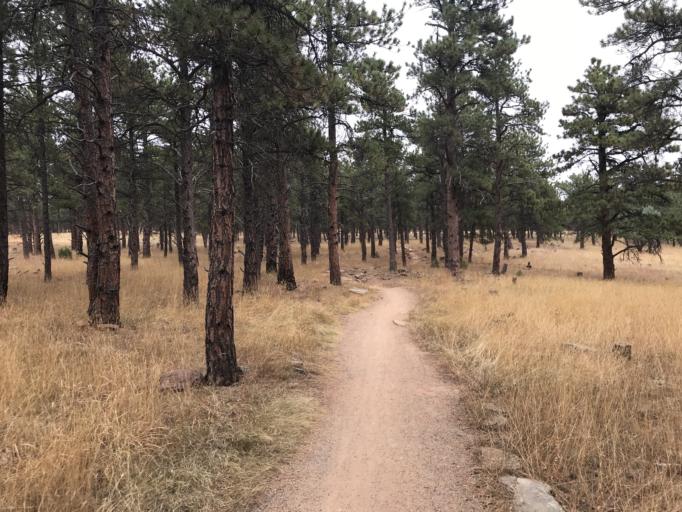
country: US
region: Colorado
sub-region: Boulder County
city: Lyons
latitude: 40.1670
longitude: -105.3005
